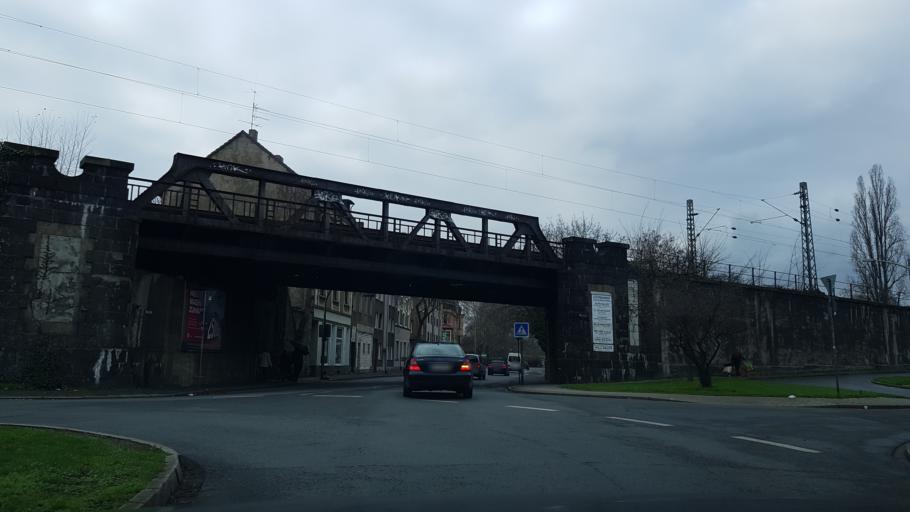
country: DE
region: North Rhine-Westphalia
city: Meiderich
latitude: 51.4706
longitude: 6.7720
